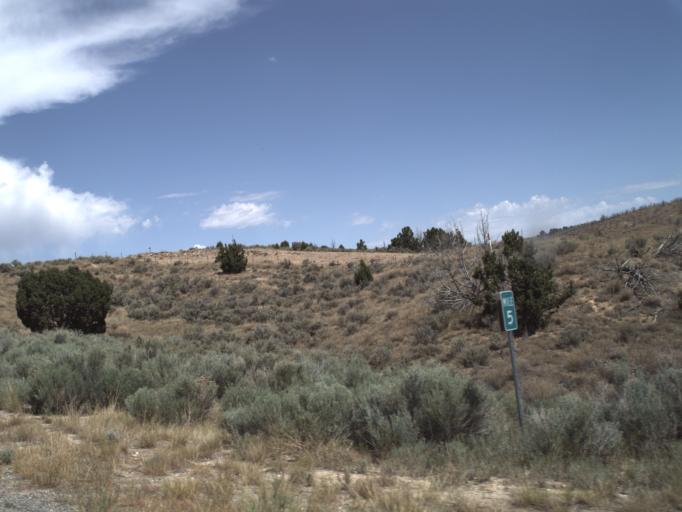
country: US
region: Utah
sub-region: Utah County
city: Genola
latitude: 39.9449
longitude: -112.2261
